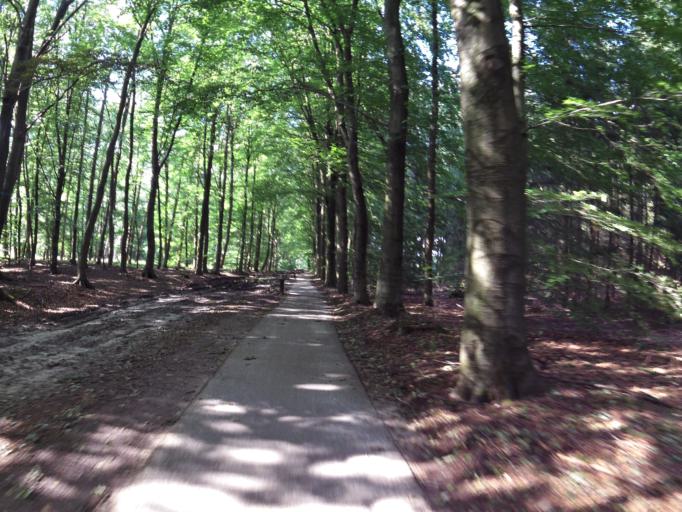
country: NL
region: North Brabant
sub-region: Gemeente Heeze-Leende
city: Heeze
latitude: 51.3922
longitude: 5.5524
